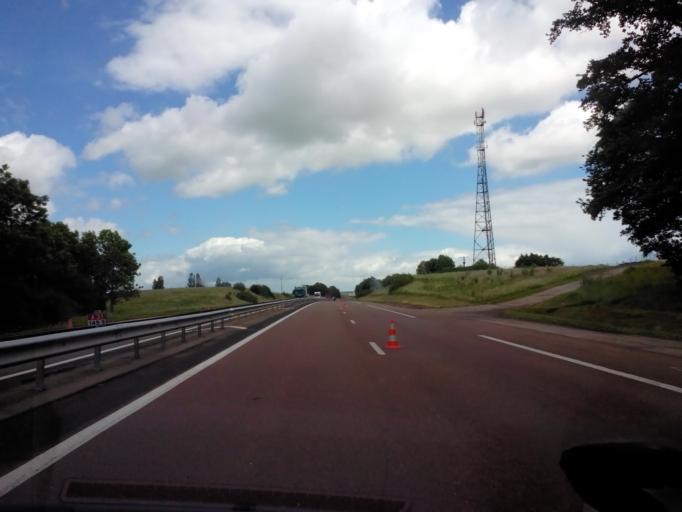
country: FR
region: Champagne-Ardenne
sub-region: Departement de la Haute-Marne
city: Saulxures
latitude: 48.0645
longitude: 5.5888
